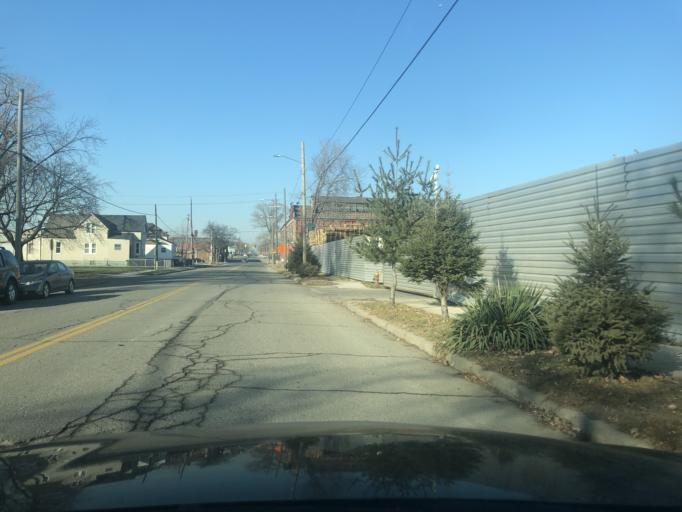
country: US
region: Michigan
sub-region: Wayne County
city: River Rouge
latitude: 42.3083
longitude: -83.0949
